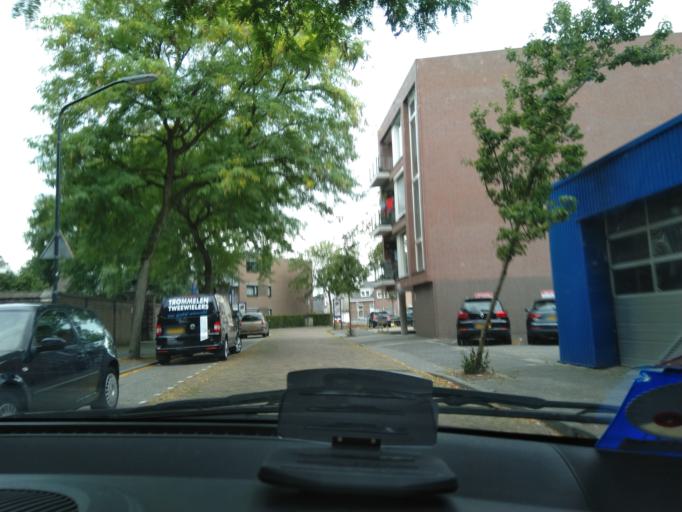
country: NL
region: North Brabant
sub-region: Gemeente Oosterhout
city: Oosterhout
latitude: 51.6418
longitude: 4.8516
